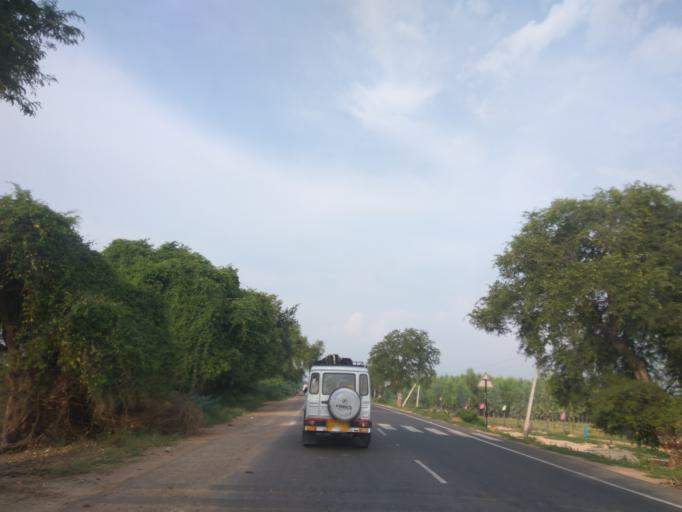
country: IN
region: Andhra Pradesh
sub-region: Guntur
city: Vinukonda
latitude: 16.0108
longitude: 79.6980
